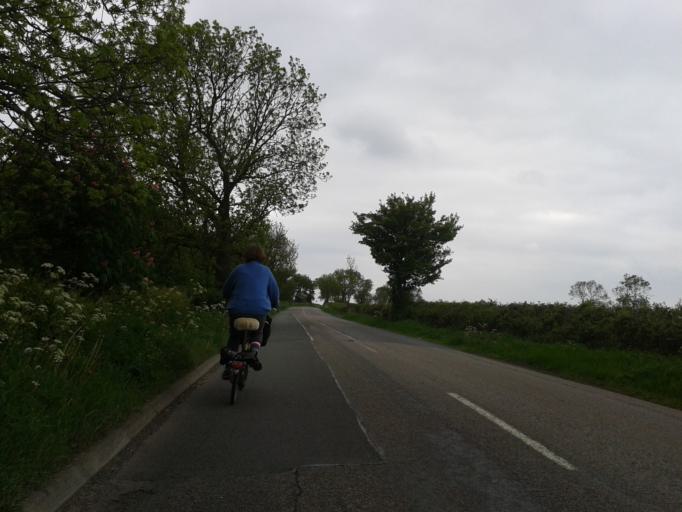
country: GB
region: England
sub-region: Leicestershire
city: Great Glen
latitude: 52.5174
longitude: -1.0574
